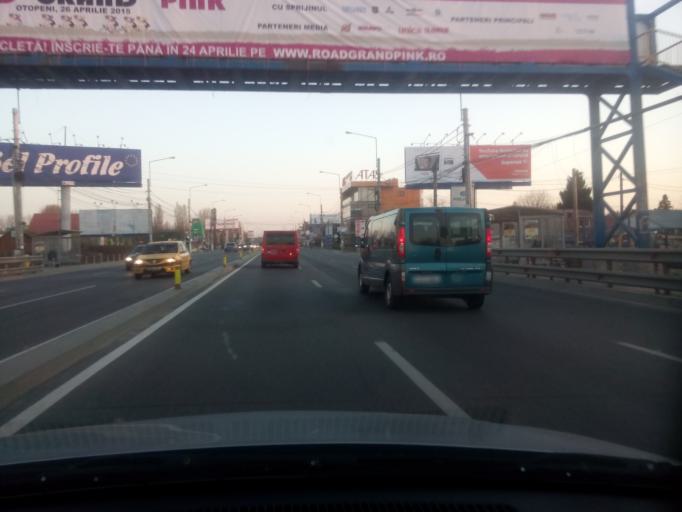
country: RO
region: Ilfov
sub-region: Comuna Otopeni
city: Otopeni
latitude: 44.5414
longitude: 26.0687
